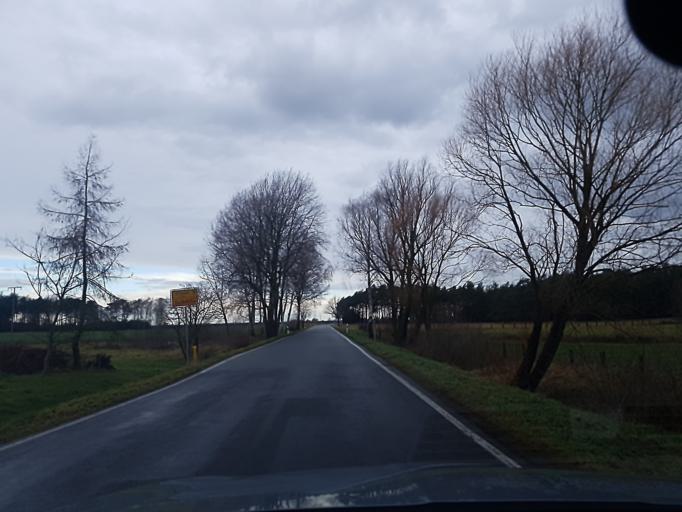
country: DE
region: Brandenburg
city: Schilda
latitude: 51.6106
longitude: 13.3817
